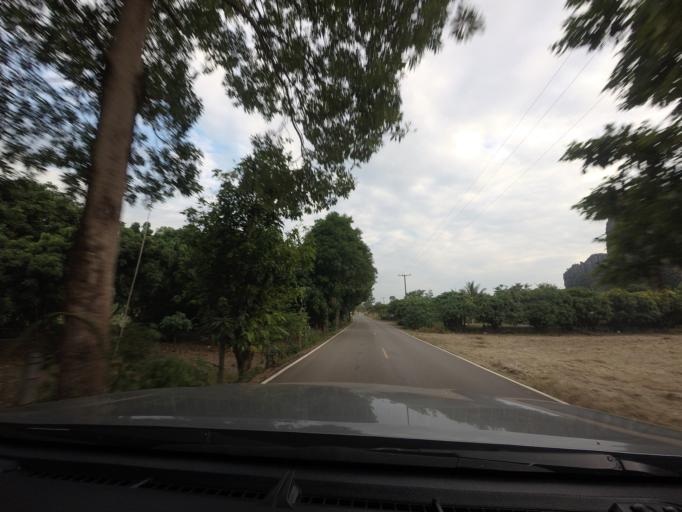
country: TH
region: Phitsanulok
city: Noen Maprang
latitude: 16.5719
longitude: 100.6859
